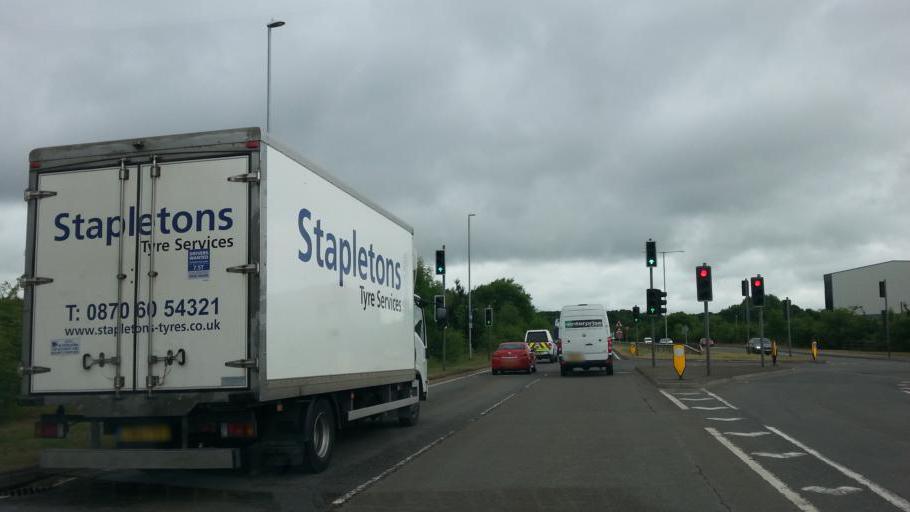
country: GB
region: England
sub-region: Northamptonshire
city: Corby
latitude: 52.4900
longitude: -0.6539
